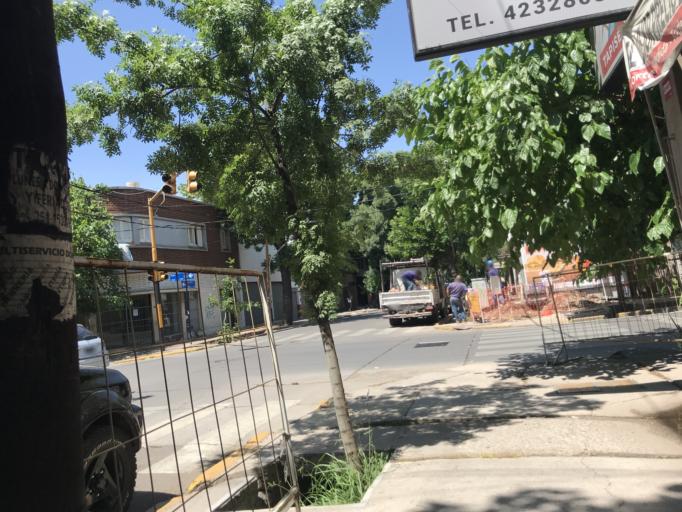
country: AR
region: Mendoza
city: Mendoza
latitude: -32.8862
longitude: -68.8344
